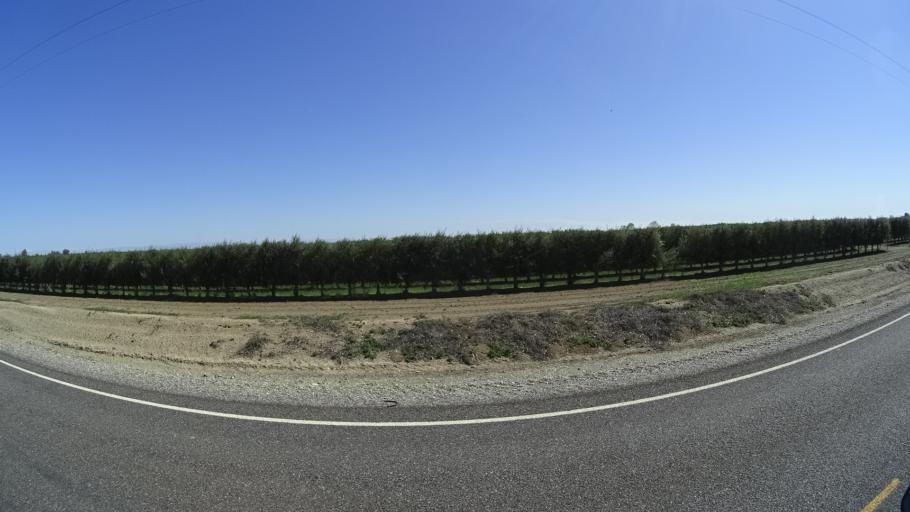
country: US
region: California
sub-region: Glenn County
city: Willows
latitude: 39.6215
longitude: -122.2500
